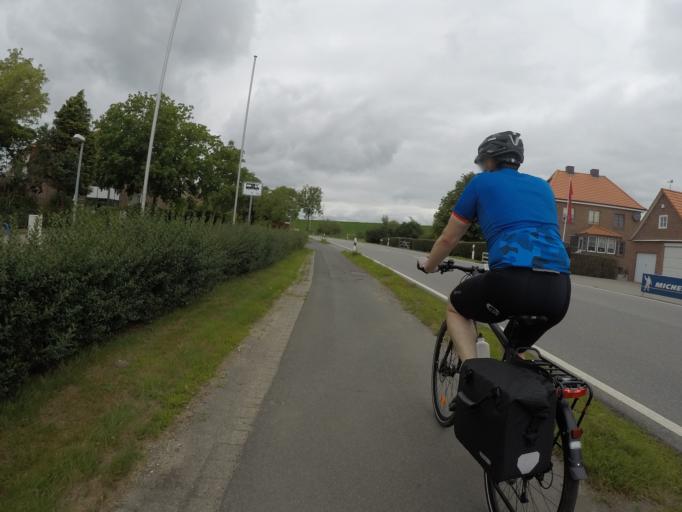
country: DE
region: Lower Saxony
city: Grunendeich
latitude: 53.5824
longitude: 9.5939
